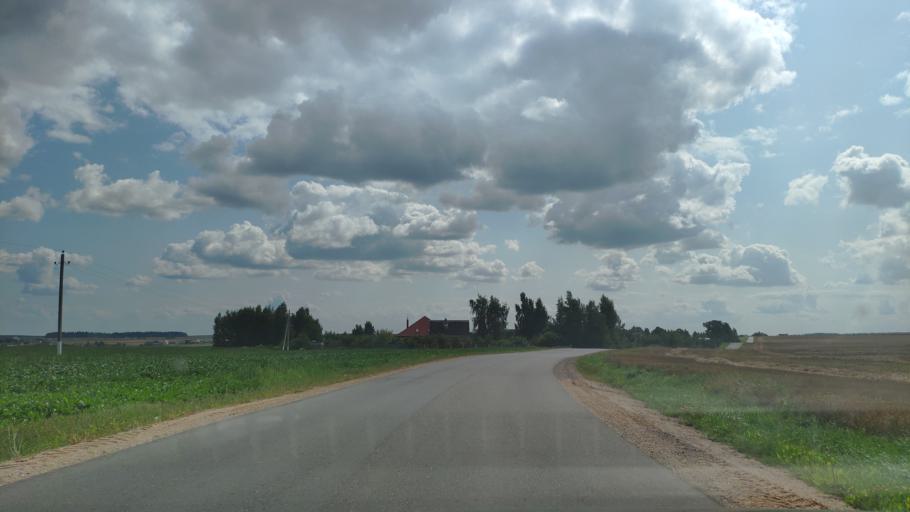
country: BY
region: Minsk
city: Khatsyezhyna
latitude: 53.8427
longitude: 27.3132
